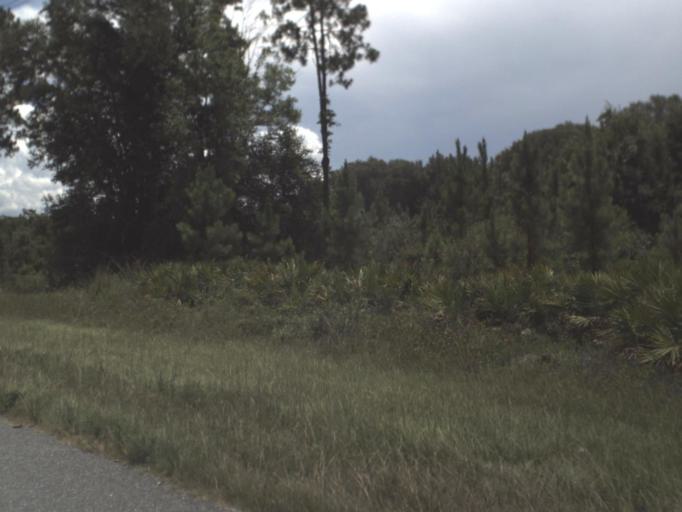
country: US
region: Florida
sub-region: Taylor County
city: Perry
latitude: 30.1426
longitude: -83.8632
